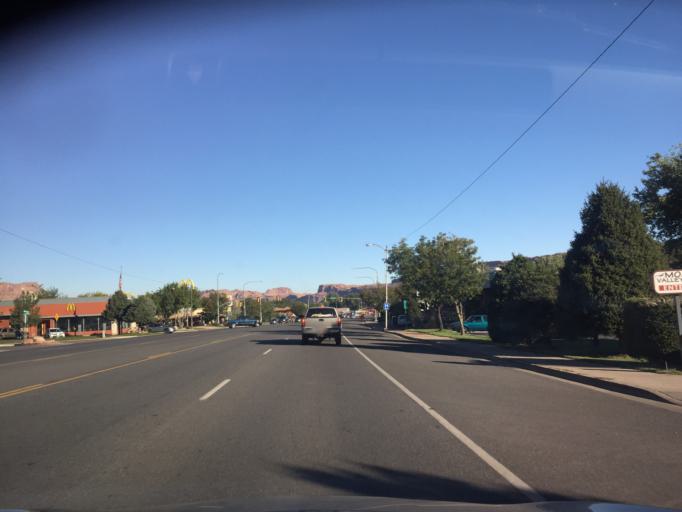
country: US
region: Utah
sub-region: Grand County
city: Moab
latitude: 38.5627
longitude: -109.5488
